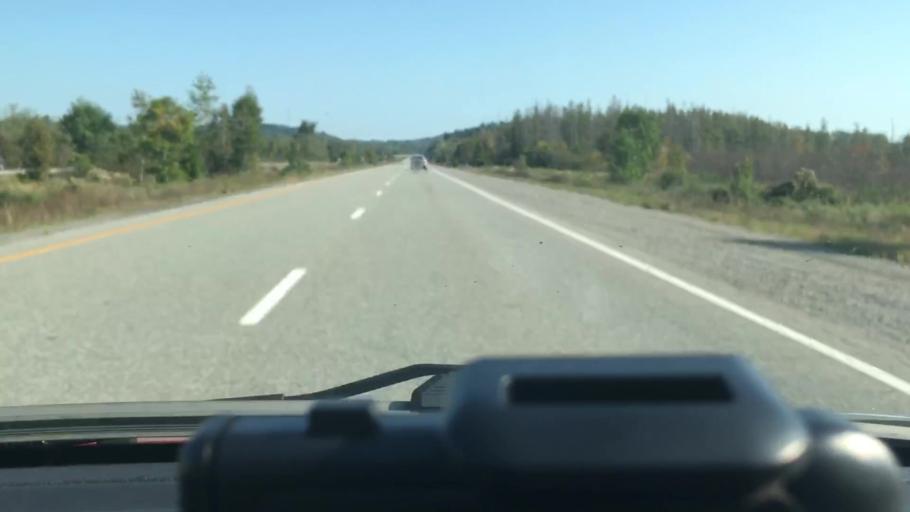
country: CA
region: Ontario
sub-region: Algoma
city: Sault Ste. Marie
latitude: 46.5129
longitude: -84.0541
